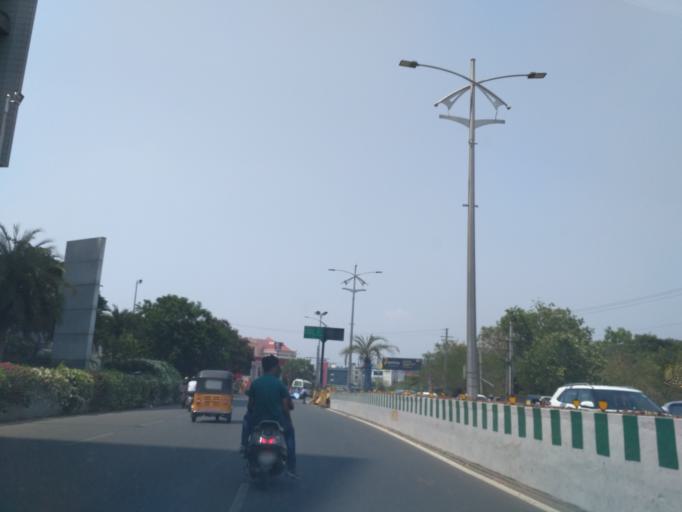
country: IN
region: Telangana
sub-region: Rangareddi
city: Kukatpalli
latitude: 17.4496
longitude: 78.3791
